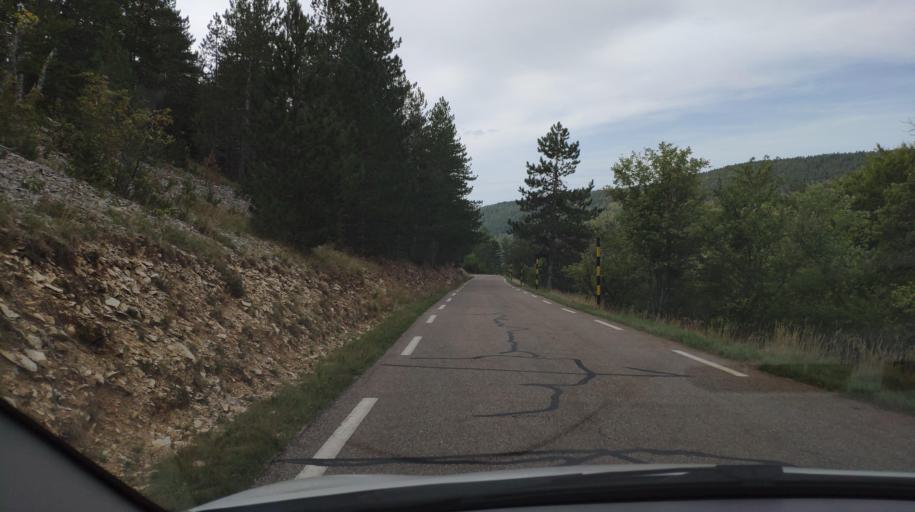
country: FR
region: Provence-Alpes-Cote d'Azur
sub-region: Departement du Vaucluse
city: Sault
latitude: 44.1491
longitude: 5.3595
